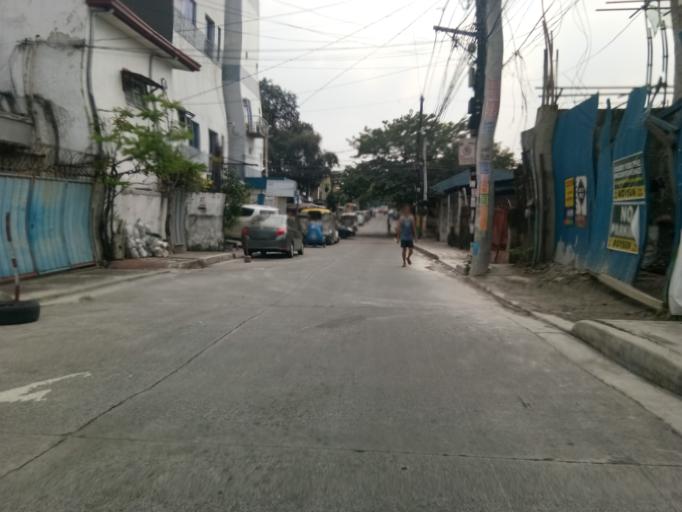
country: PH
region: Metro Manila
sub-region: Pasig
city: Pasig City
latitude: 14.6136
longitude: 121.0568
